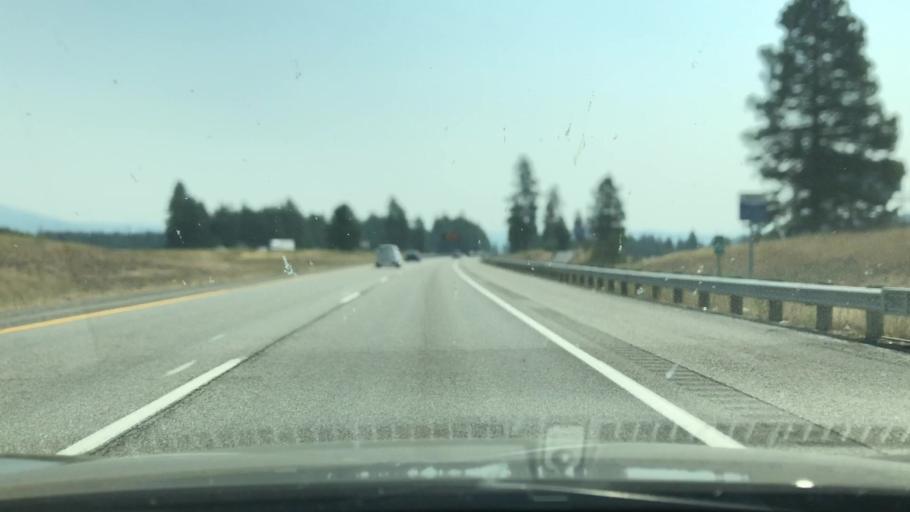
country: US
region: Idaho
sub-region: Kootenai County
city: Coeur d'Alene
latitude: 47.7081
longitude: -116.8554
